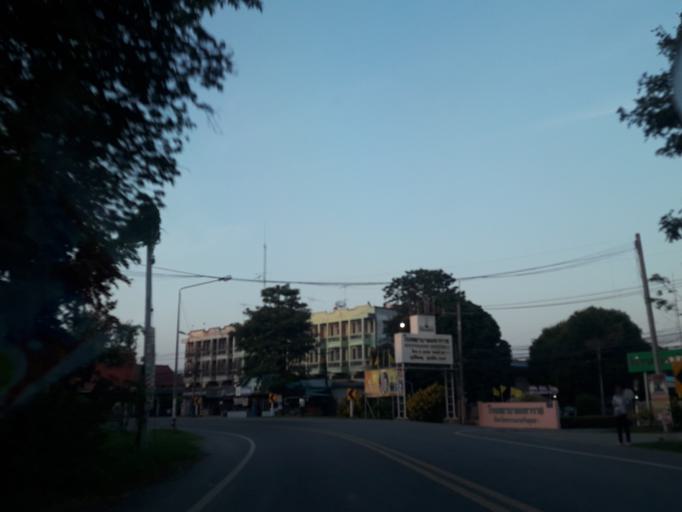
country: TH
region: Phra Nakhon Si Ayutthaya
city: Maha Rat
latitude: 14.5382
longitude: 100.5296
